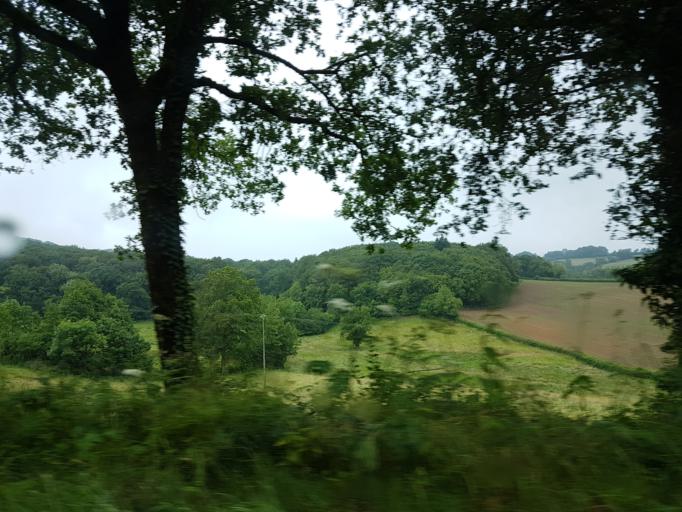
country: FR
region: Bourgogne
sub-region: Departement de la Nievre
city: Chateau-Chinon(Ville)
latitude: 47.1574
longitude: 3.8632
